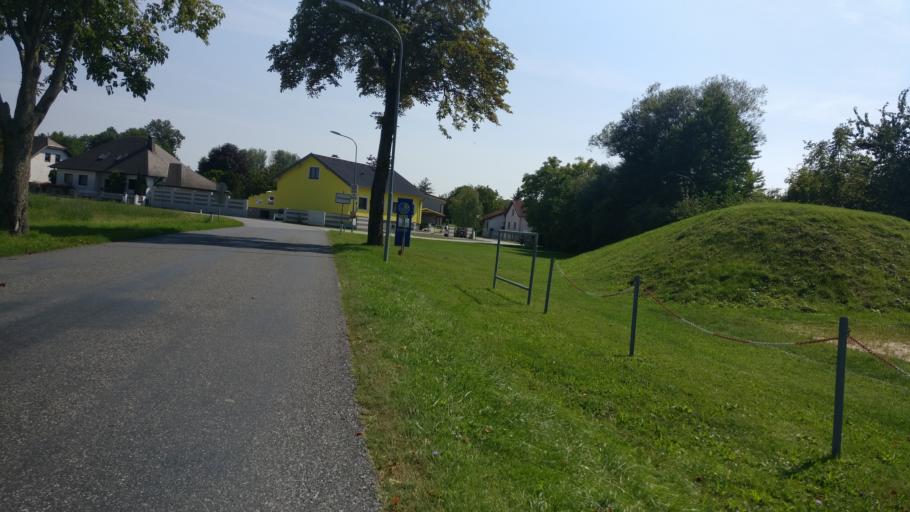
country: AT
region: Lower Austria
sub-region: Politischer Bezirk Baden
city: Mitterndorf an der Fischa
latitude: 47.9792
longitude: 16.4391
